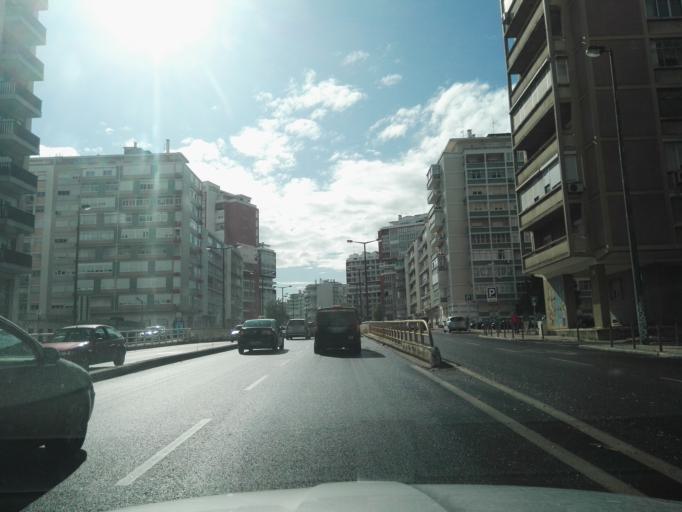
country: PT
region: Lisbon
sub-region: Lisbon
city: Lisbon
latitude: 38.7492
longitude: -9.1392
